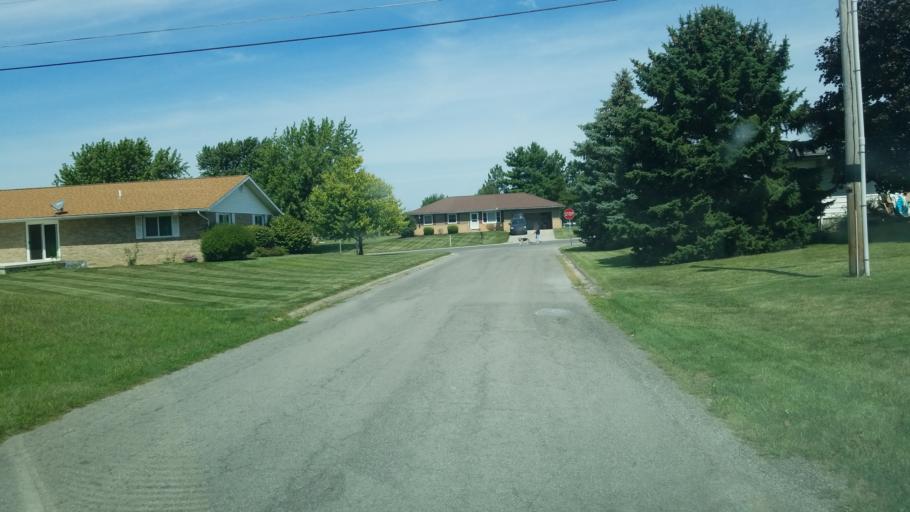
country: US
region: Ohio
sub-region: Hardin County
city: Kenton
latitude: 40.6619
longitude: -83.6014
